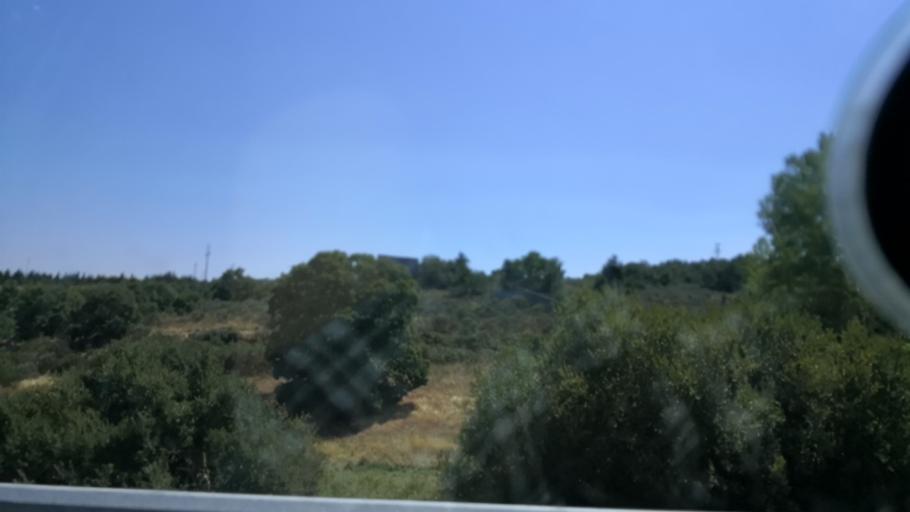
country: PT
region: Braganca
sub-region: Braganca Municipality
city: Braganca
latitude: 41.7687
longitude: -6.7924
